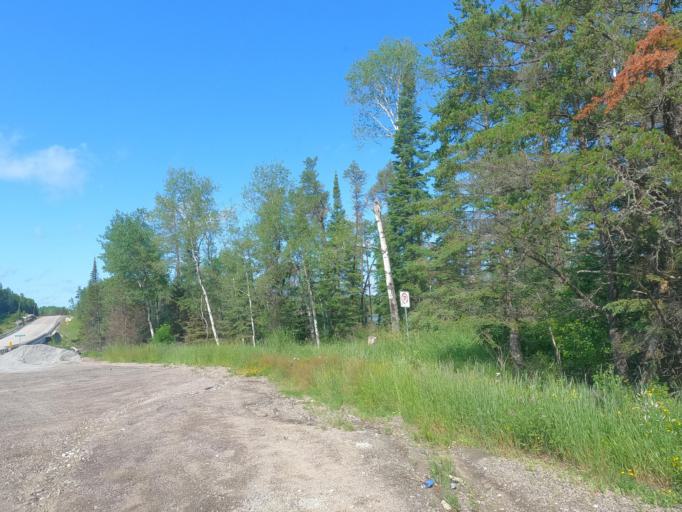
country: CA
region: Ontario
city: Dryden
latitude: 49.9267
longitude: -93.3521
